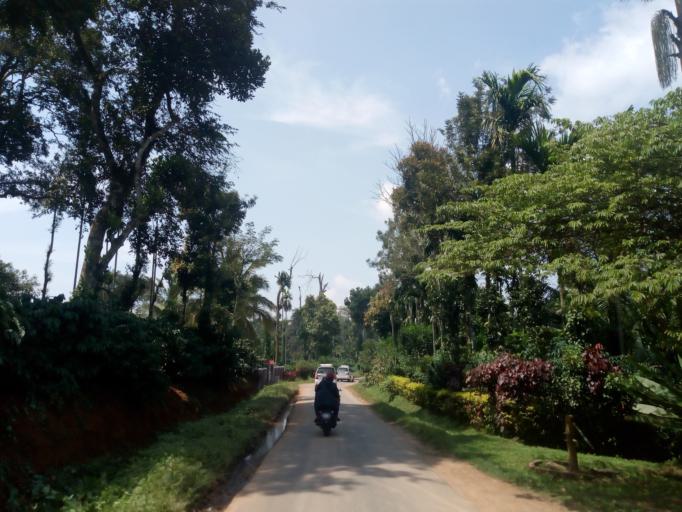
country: IN
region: Karnataka
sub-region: Kodagu
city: Ponnampet
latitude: 12.0308
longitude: 75.9584
